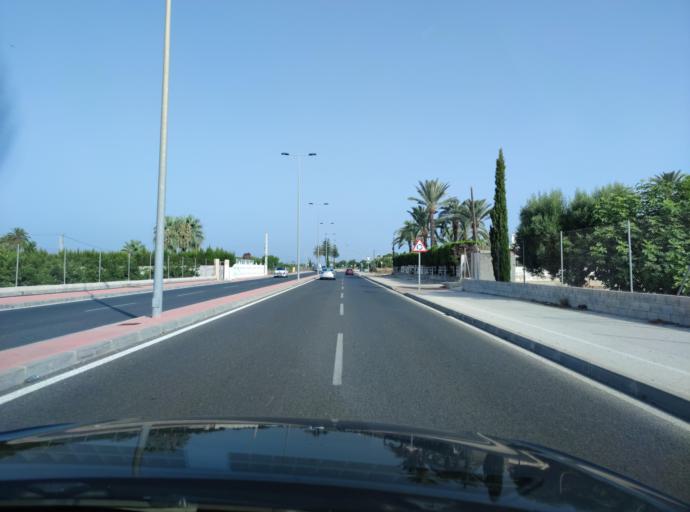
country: ES
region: Valencia
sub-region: Provincia de Alicante
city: Santa Pola
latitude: 38.2040
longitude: -0.5774
